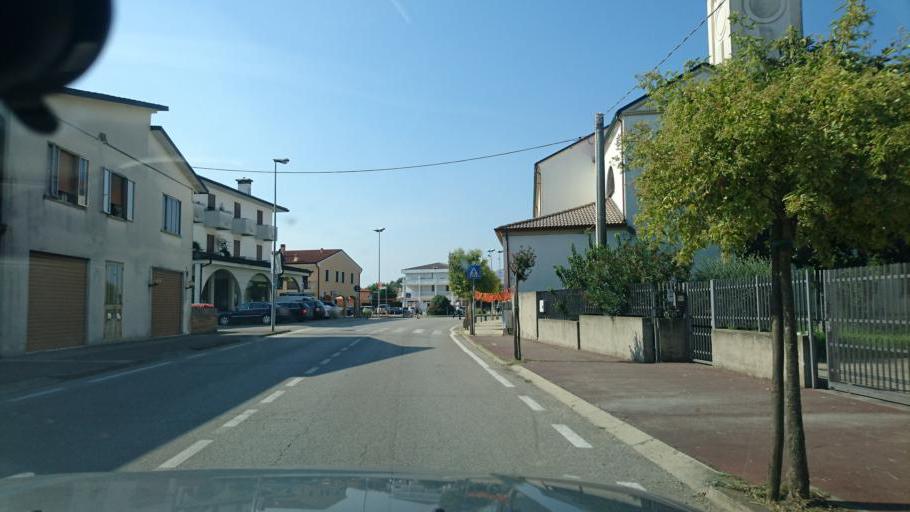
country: IT
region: Veneto
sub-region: Provincia di Padova
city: Terrassa Padovana
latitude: 45.2458
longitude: 11.9025
